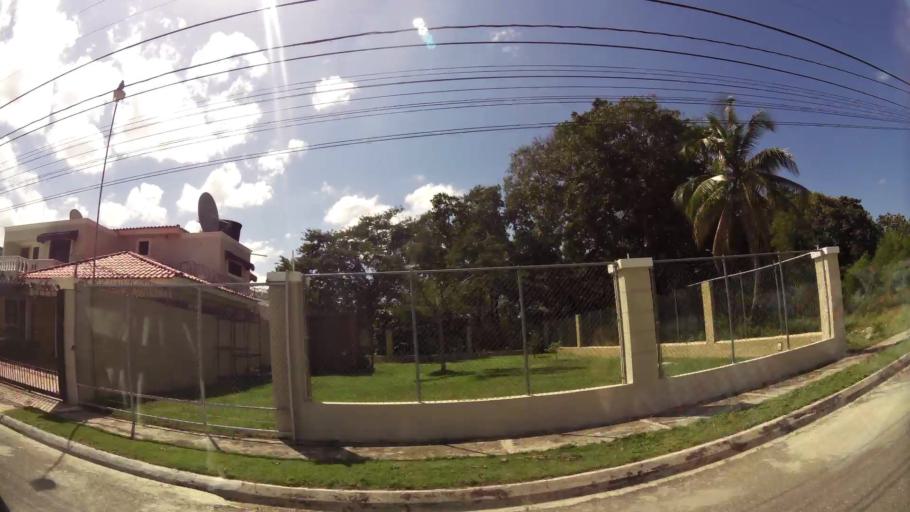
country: DO
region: San Cristobal
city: San Cristobal
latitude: 18.4337
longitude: -70.1298
